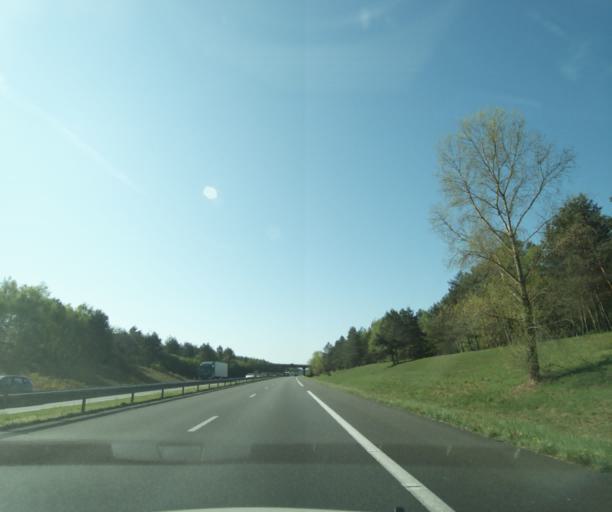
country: FR
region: Centre
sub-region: Departement du Loiret
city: Saint-Hilaire-Saint-Mesmin
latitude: 47.8250
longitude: 1.8594
